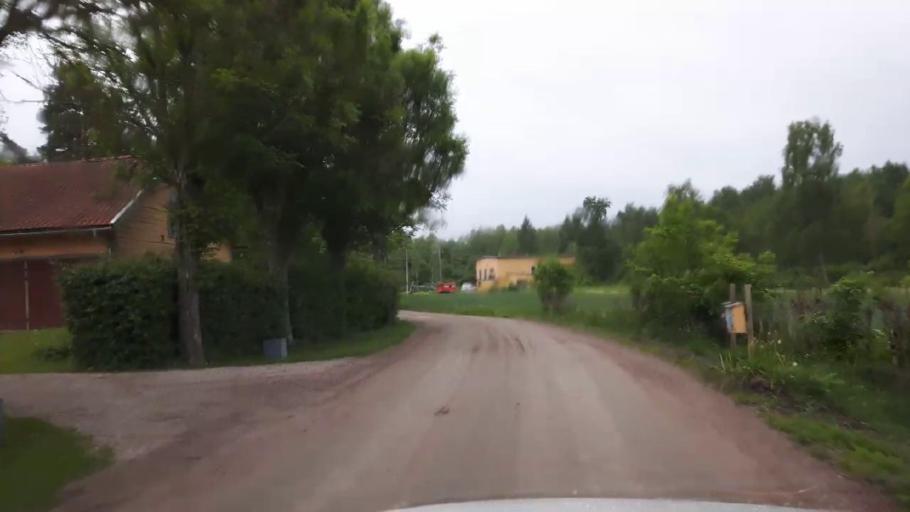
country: SE
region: Vaestmanland
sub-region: Arboga Kommun
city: Tyringe
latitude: 59.3811
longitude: 15.9371
